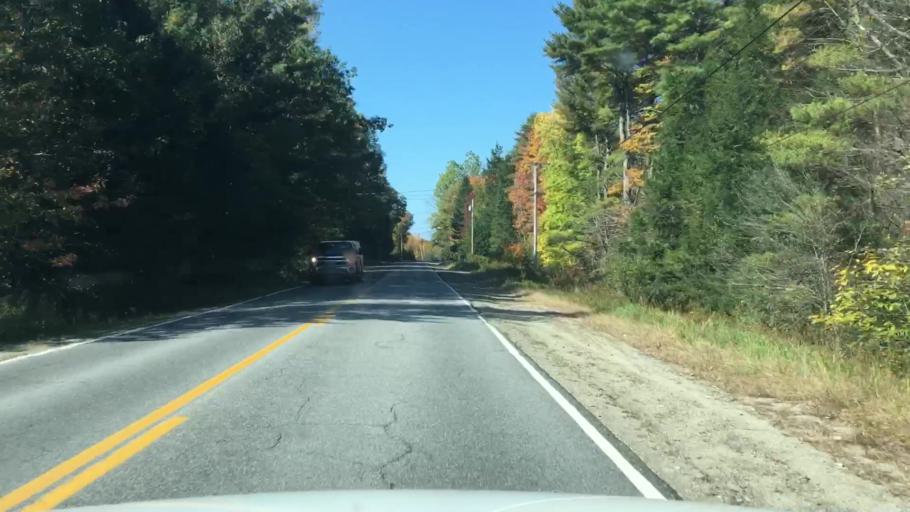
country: US
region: Maine
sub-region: Androscoggin County
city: Lisbon Falls
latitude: 44.0369
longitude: -69.9781
